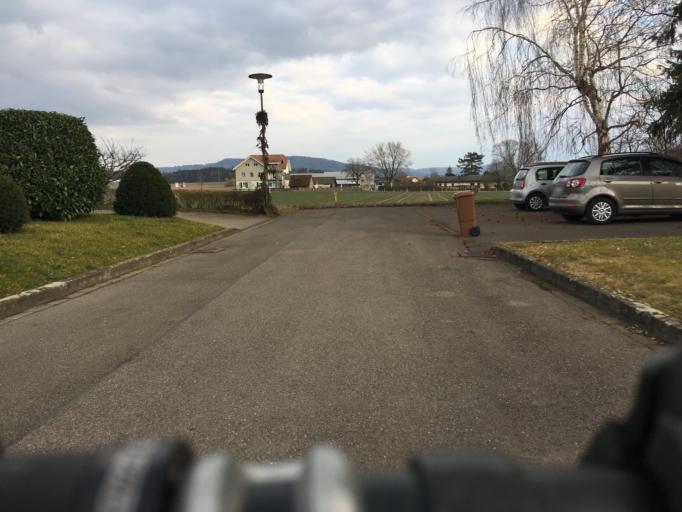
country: DE
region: Baden-Wuerttemberg
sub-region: Freiburg Region
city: Gottmadingen
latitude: 47.7280
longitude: 8.7826
